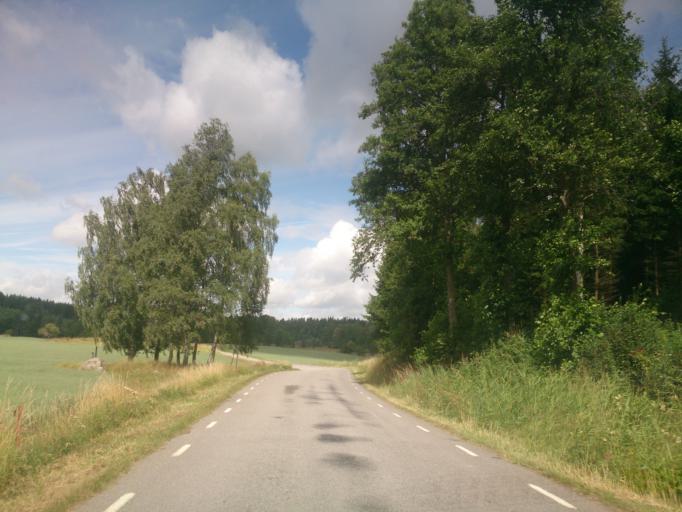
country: SE
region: OEstergoetland
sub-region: Atvidabergs Kommun
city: Atvidaberg
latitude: 58.3209
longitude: 16.0533
